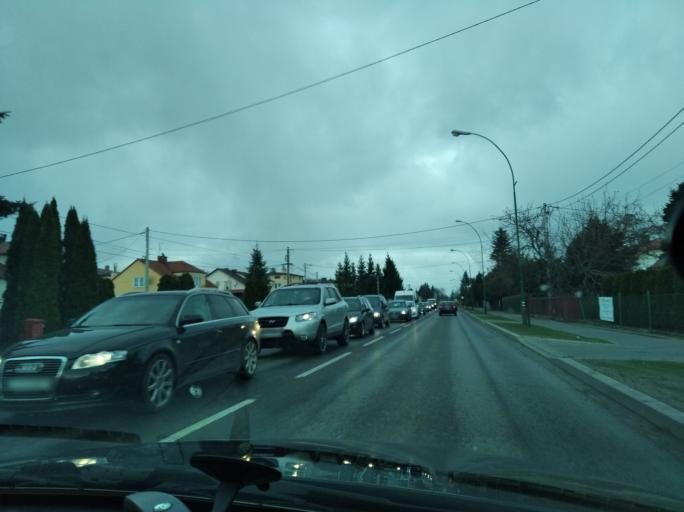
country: PL
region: Subcarpathian Voivodeship
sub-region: Powiat lancucki
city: Lancut
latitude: 50.0854
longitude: 22.2324
